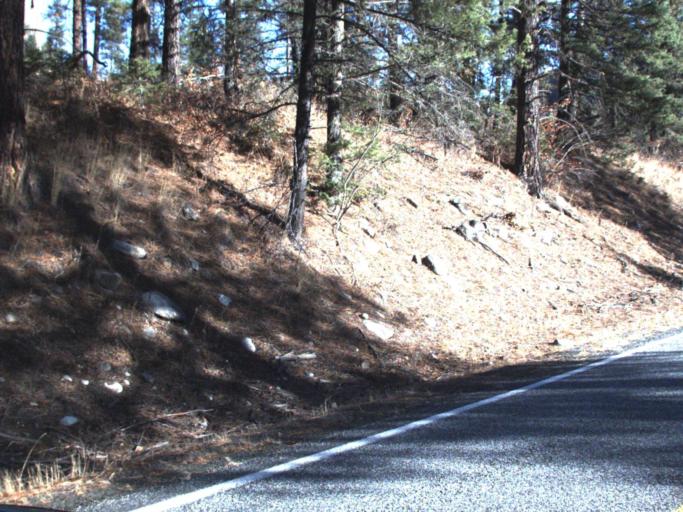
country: US
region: Washington
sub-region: Ferry County
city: Republic
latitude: 48.4194
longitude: -118.7339
